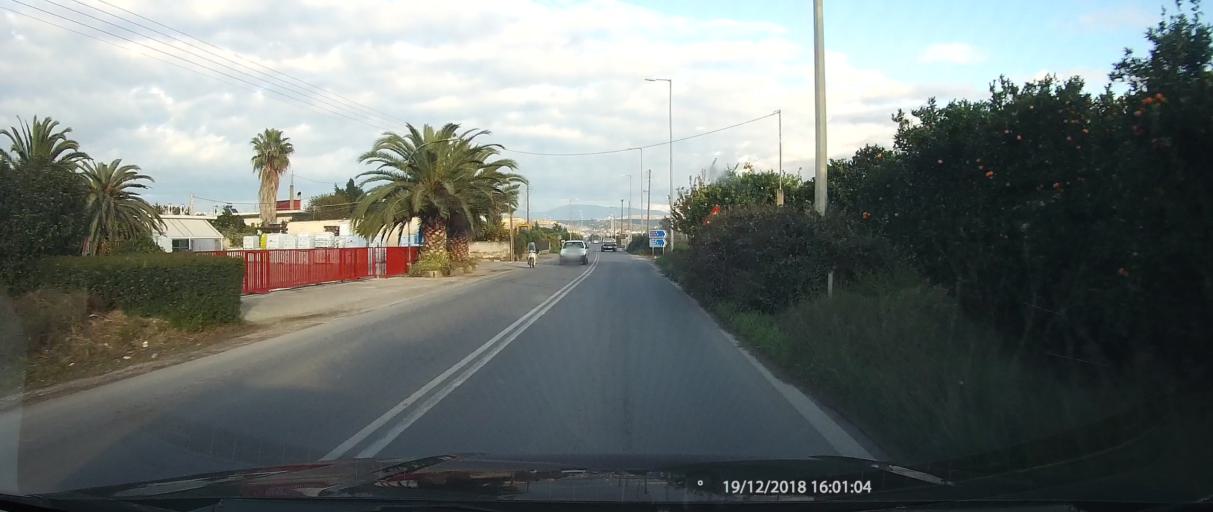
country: GR
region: Peloponnese
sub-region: Nomos Lakonias
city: Skala
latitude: 36.8556
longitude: 22.6839
